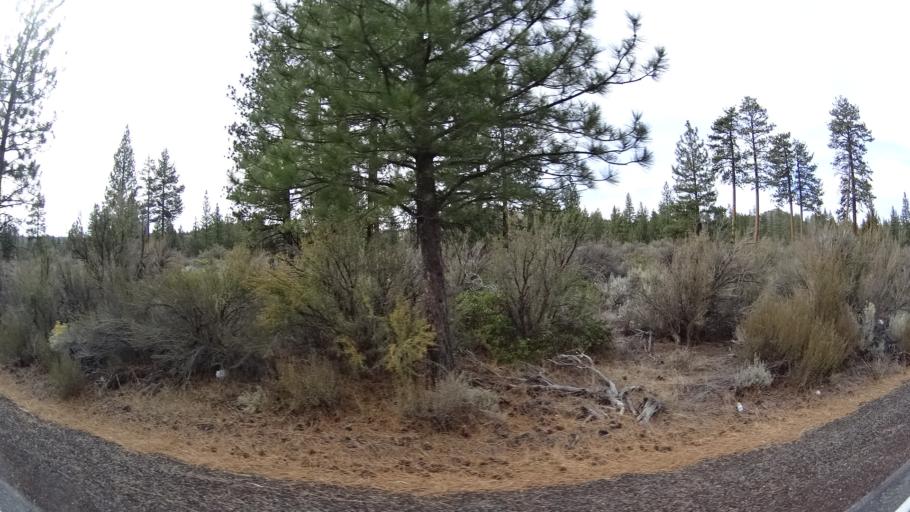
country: US
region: California
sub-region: Siskiyou County
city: Weed
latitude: 41.5413
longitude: -122.2455
